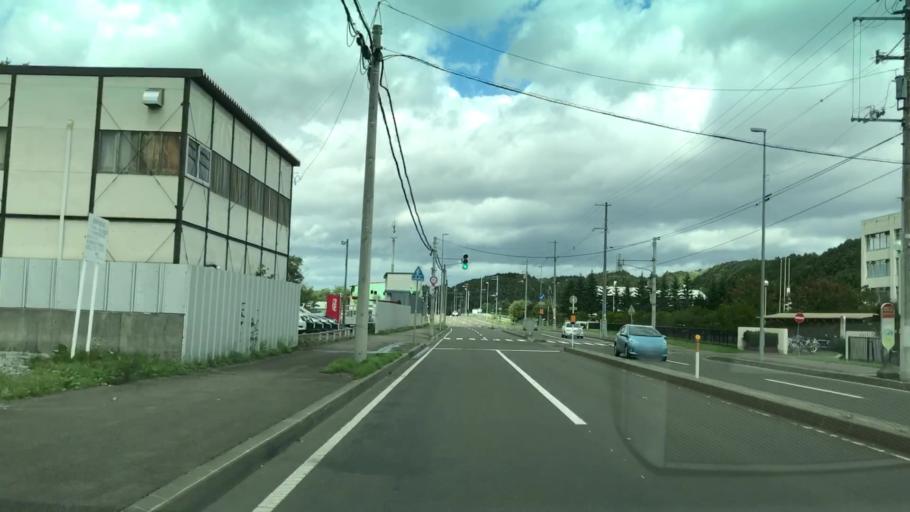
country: JP
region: Hokkaido
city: Kitahiroshima
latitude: 42.9713
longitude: 141.4518
